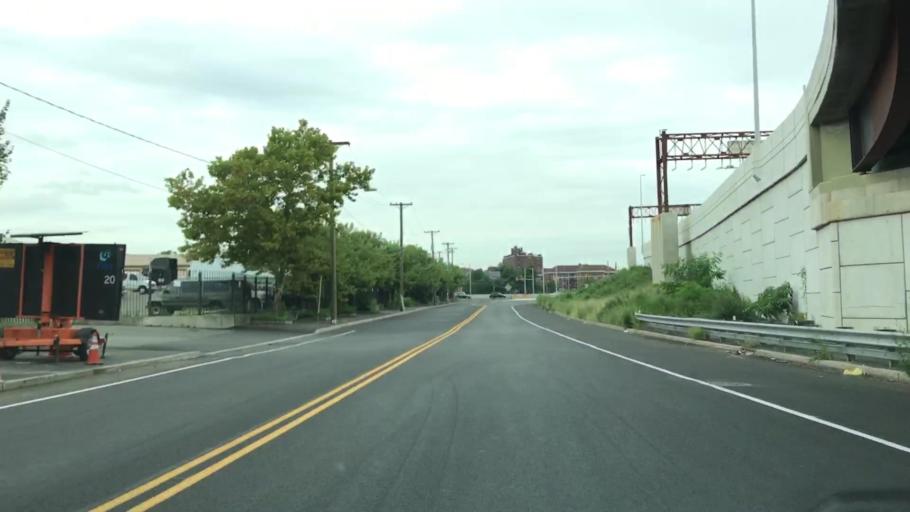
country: US
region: New Jersey
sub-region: Hudson County
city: Bayonne
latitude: 40.6790
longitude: -74.0975
